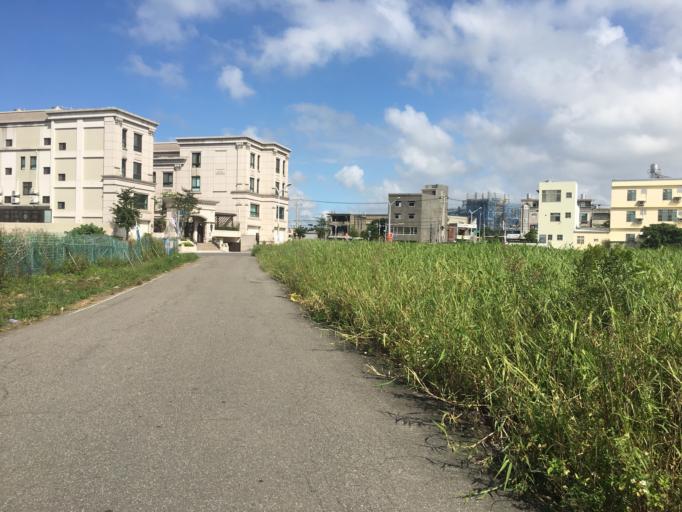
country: TW
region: Taiwan
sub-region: Hsinchu
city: Zhubei
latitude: 24.8900
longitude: 121.0500
